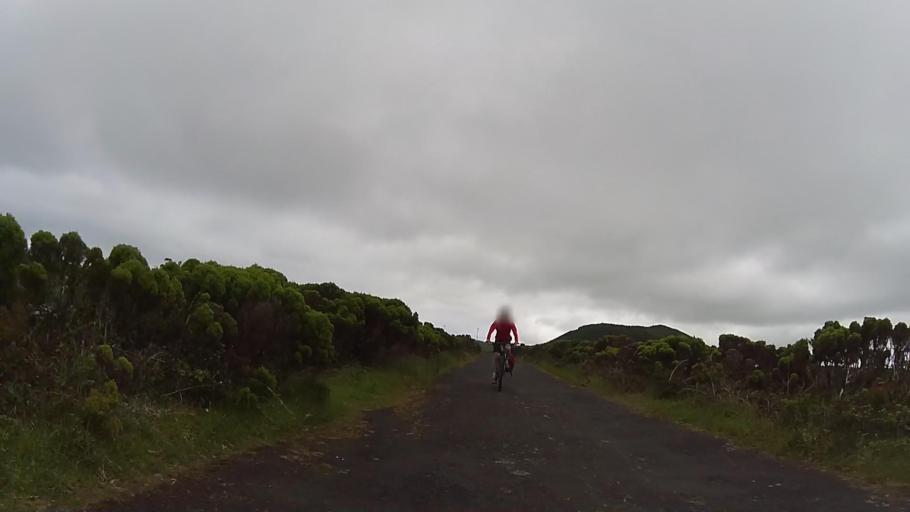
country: PT
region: Azores
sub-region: Sao Roque do Pico
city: Sao Roque do Pico
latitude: 38.4640
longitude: -28.2841
